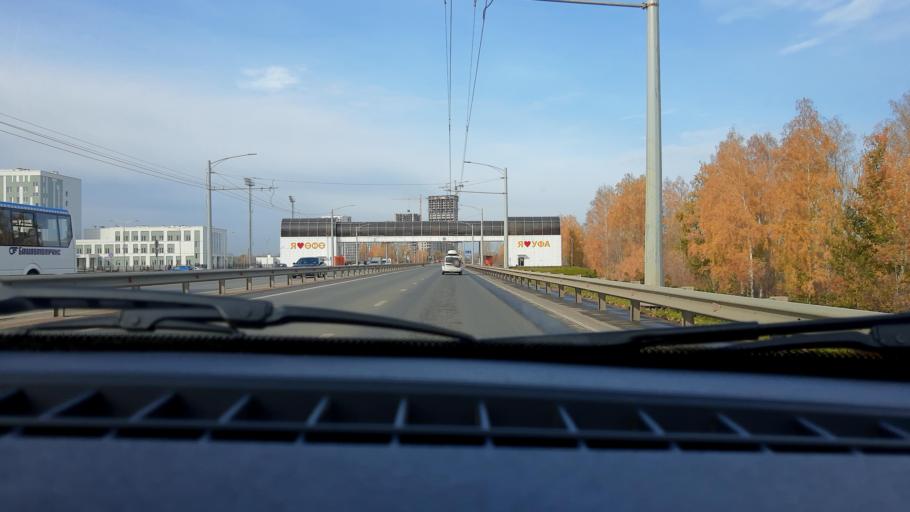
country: RU
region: Bashkortostan
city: Mikhaylovka
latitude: 54.7693
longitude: 55.9157
